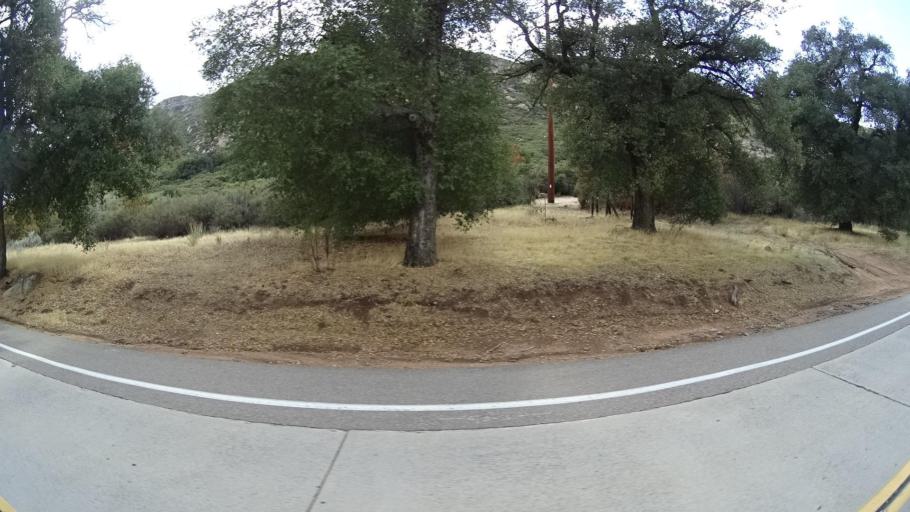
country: US
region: California
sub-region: San Diego County
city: Pine Valley
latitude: 32.8000
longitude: -116.5002
